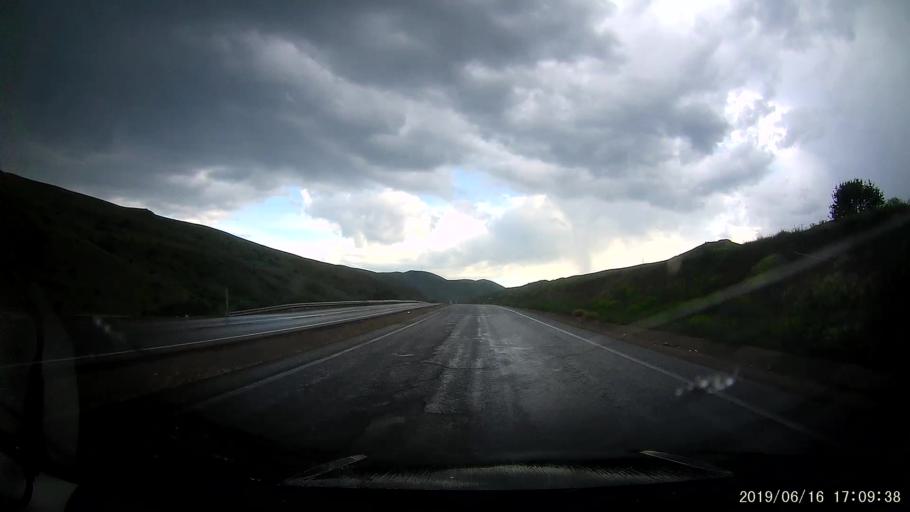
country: TR
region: Erzurum
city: Askale
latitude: 39.8922
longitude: 40.6482
